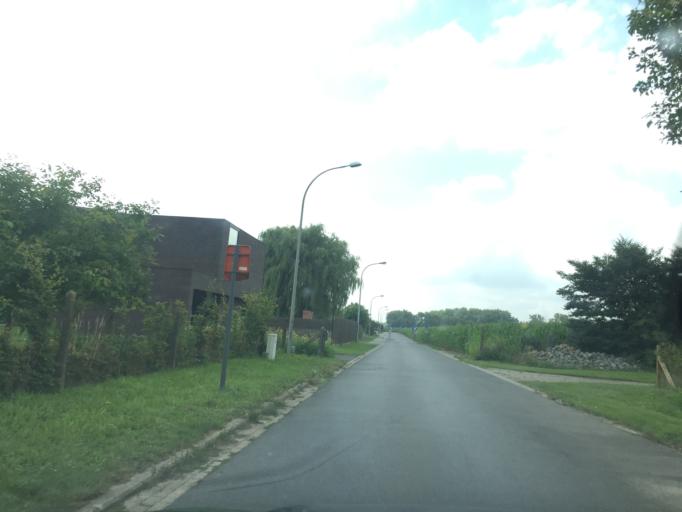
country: BE
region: Flanders
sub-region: Provincie West-Vlaanderen
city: Kortemark
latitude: 51.0317
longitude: 3.0271
